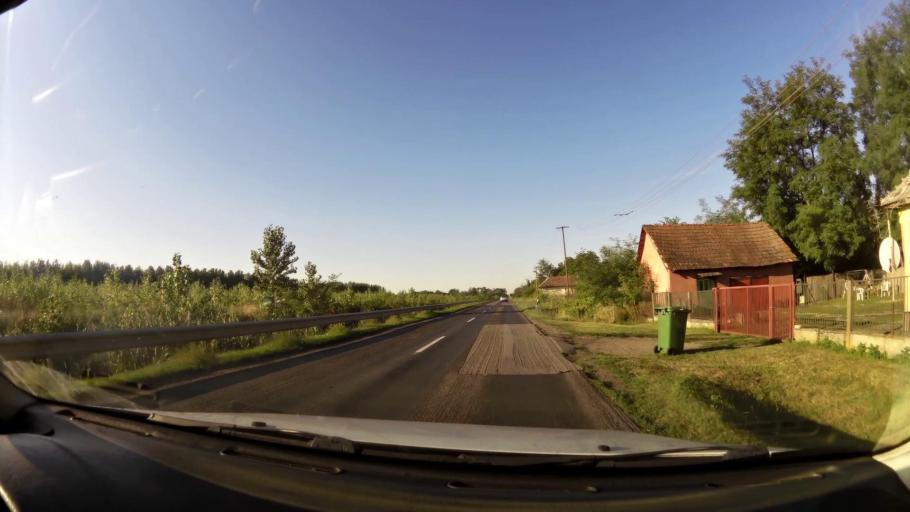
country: HU
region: Pest
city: Tapioszolos
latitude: 47.2789
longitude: 19.8657
